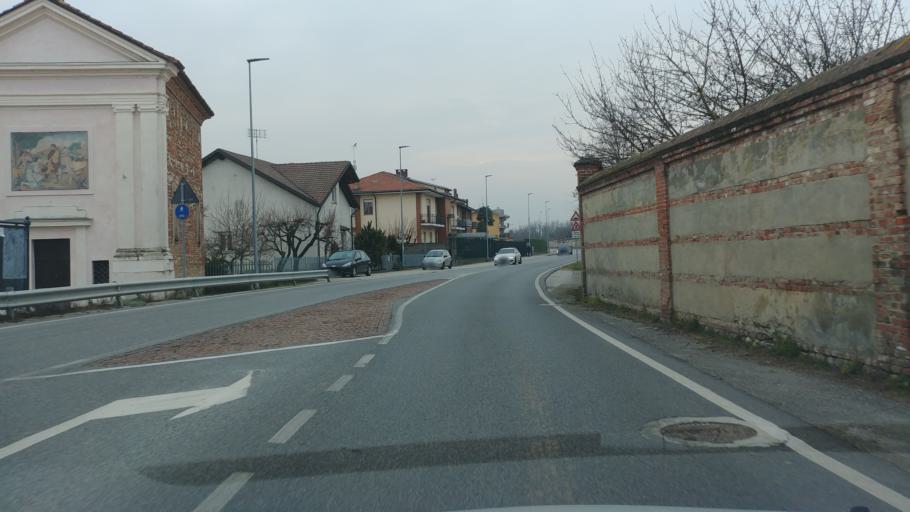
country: IT
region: Piedmont
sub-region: Provincia di Cuneo
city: Fossano
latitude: 44.5346
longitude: 7.7120
